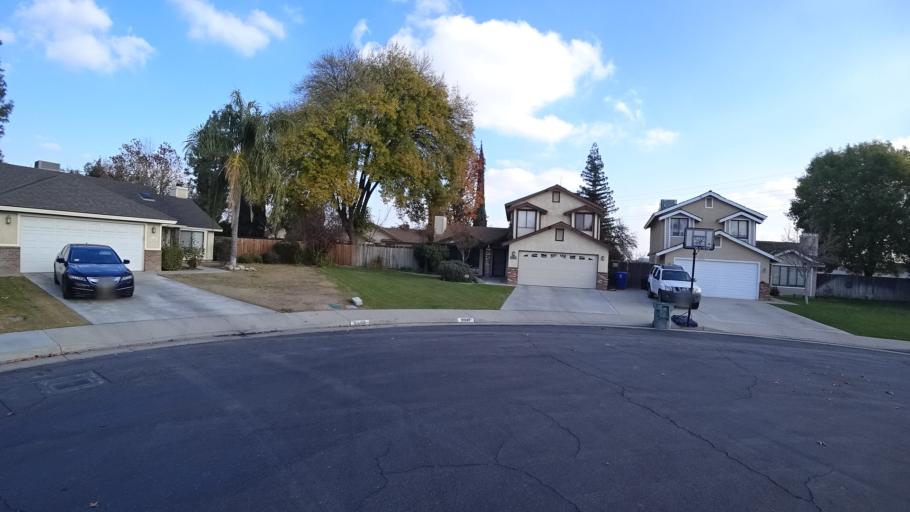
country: US
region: California
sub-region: Kern County
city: Greenacres
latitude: 35.3113
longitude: -119.1027
